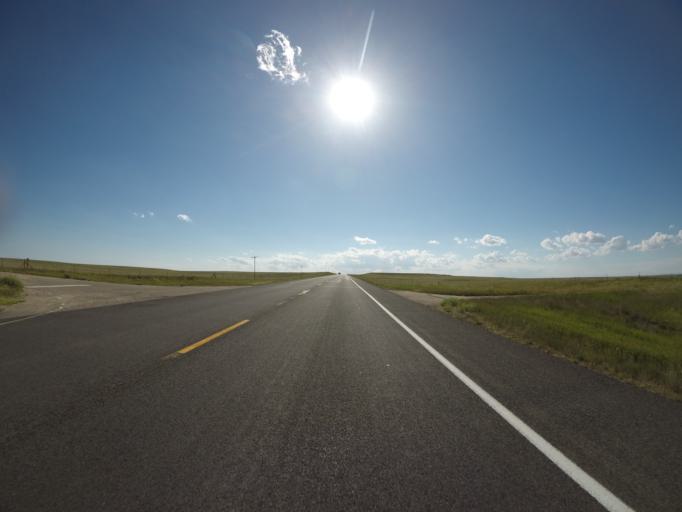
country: US
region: Colorado
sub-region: Morgan County
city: Brush
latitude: 40.6103
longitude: -103.6386
